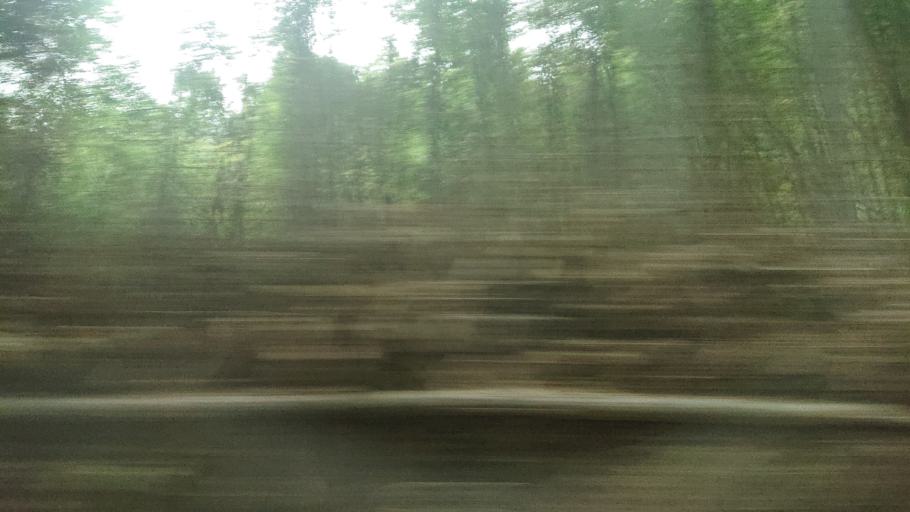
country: TW
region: Taiwan
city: Lugu
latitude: 23.6241
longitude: 120.7135
